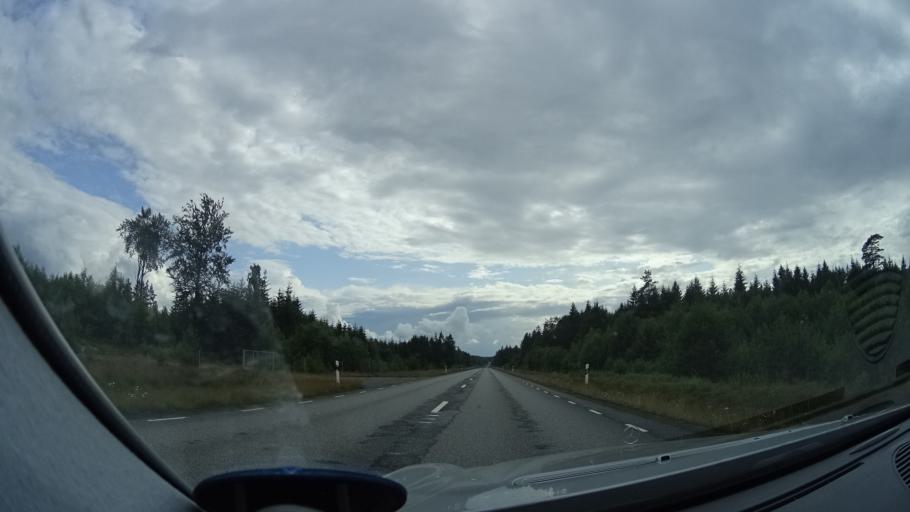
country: SE
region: Blekinge
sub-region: Karlshamns Kommun
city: Svangsta
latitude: 56.2725
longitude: 14.8577
